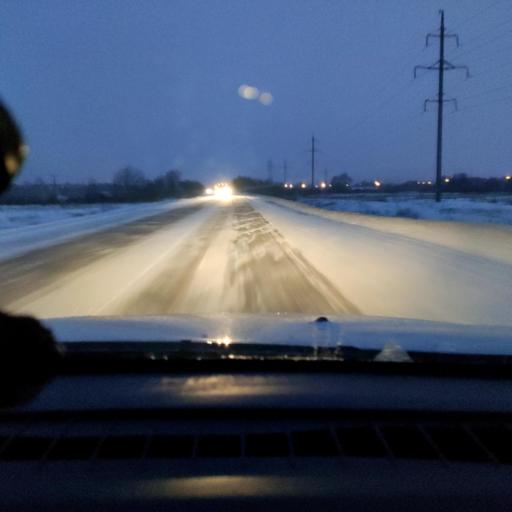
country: RU
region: Samara
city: Kinel'-Cherkassy
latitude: 53.4490
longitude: 51.5249
